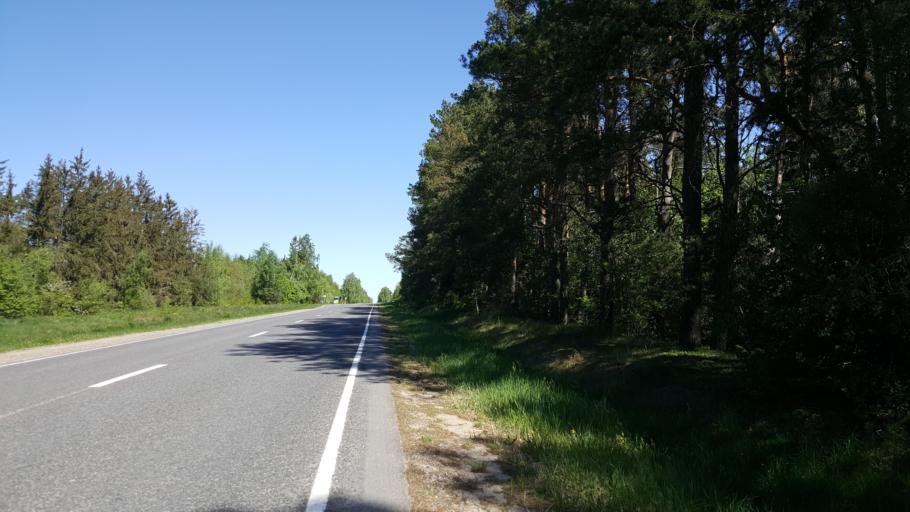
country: BY
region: Brest
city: Kamyanyets
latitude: 52.4566
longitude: 23.7827
